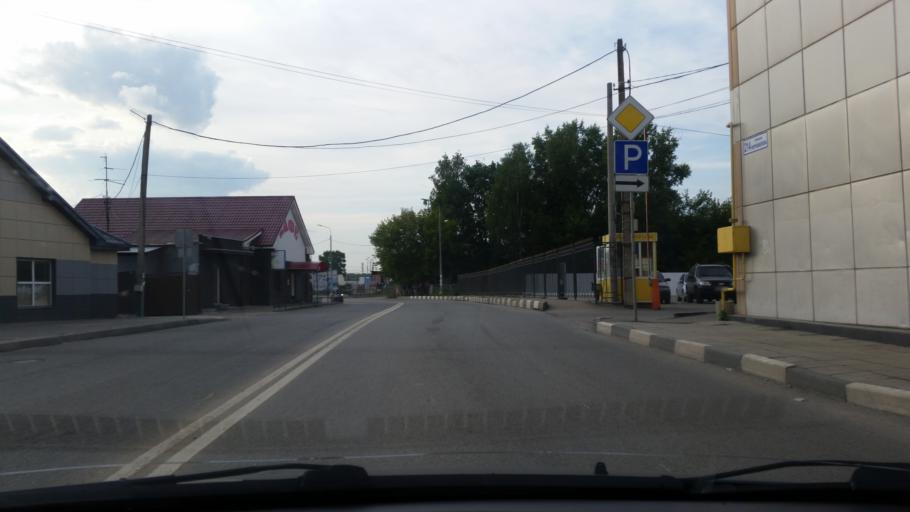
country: RU
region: Moskovskaya
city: Serpukhov
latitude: 54.9353
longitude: 37.4499
